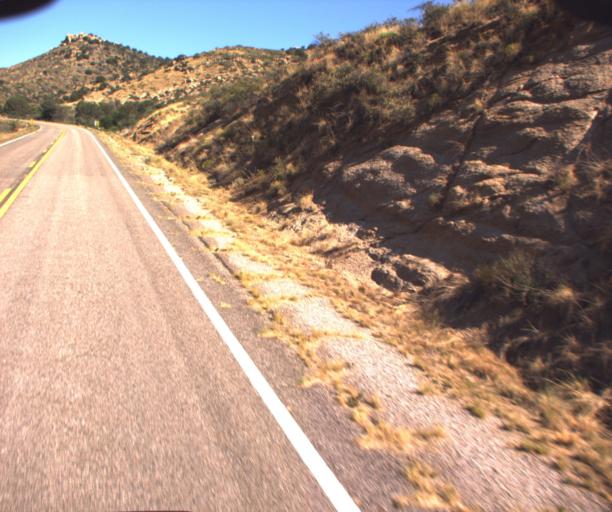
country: US
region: Arizona
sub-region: Graham County
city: Swift Trail Junction
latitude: 32.5733
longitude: -109.8332
